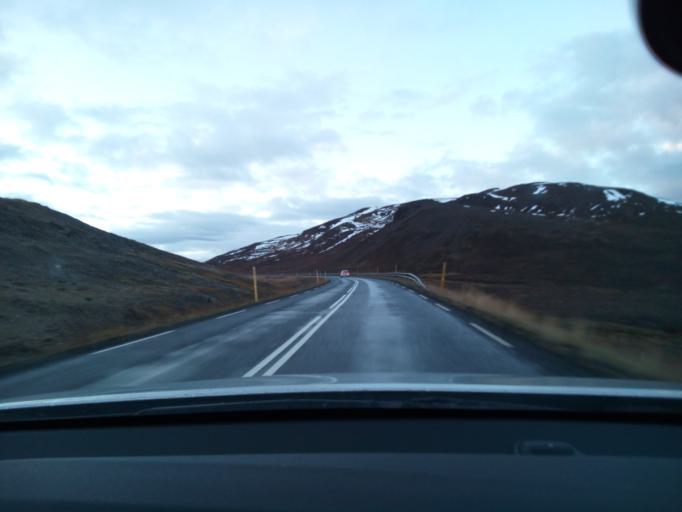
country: IS
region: Northeast
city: Akureyri
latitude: 65.8008
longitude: -17.9501
